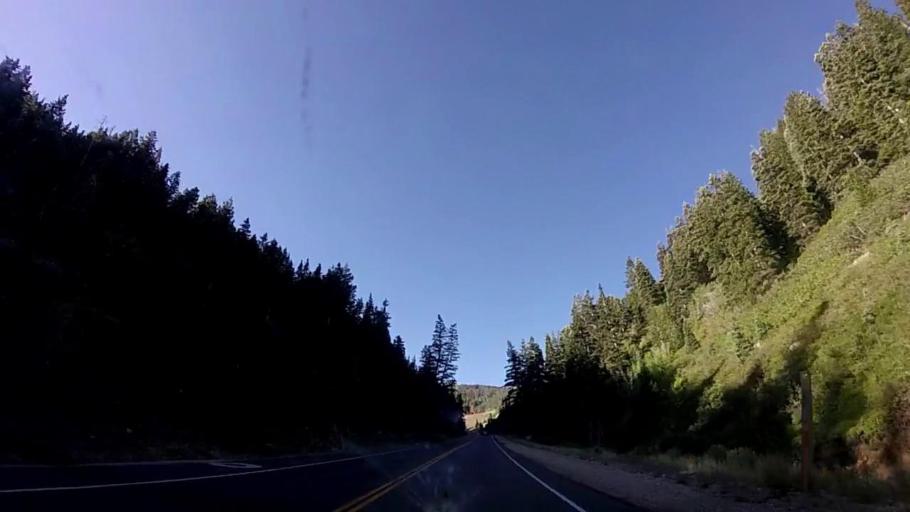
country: US
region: Utah
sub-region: Summit County
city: Park City
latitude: 40.6313
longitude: -111.4951
